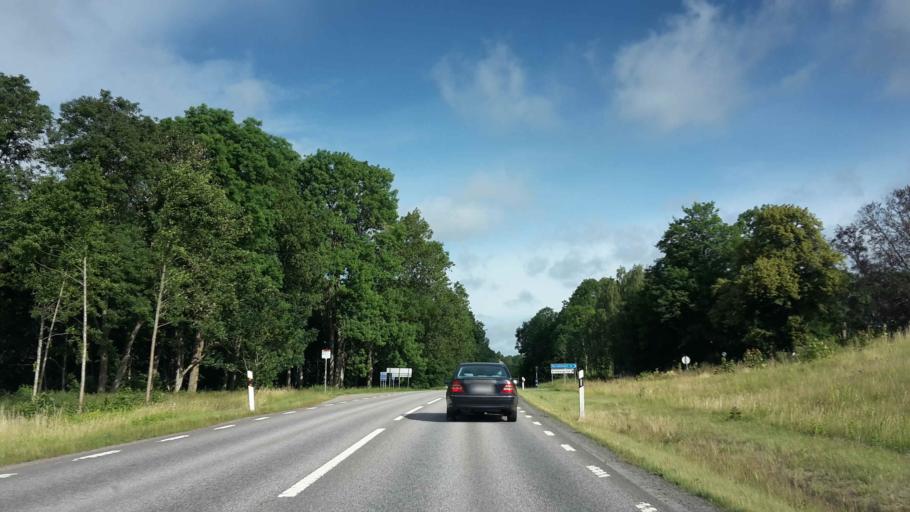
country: SE
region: OEstergoetland
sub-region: Motala Kommun
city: Borensberg
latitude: 58.5760
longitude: 15.2078
